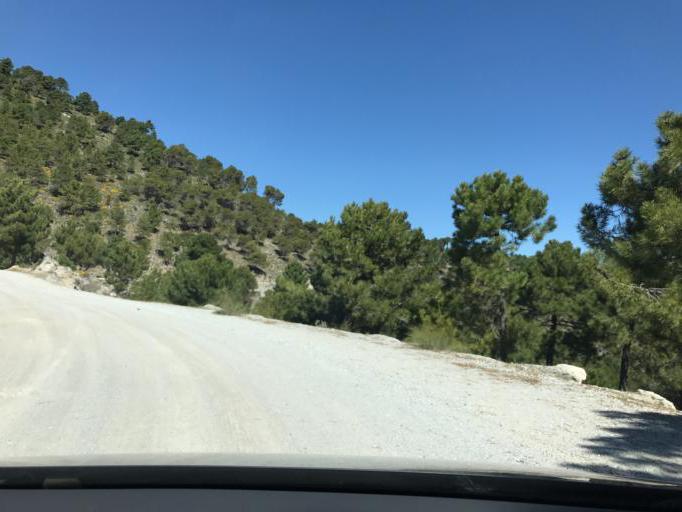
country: ES
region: Andalusia
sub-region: Provincia de Granada
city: Huetor Santillan
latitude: 37.2415
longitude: -3.5223
